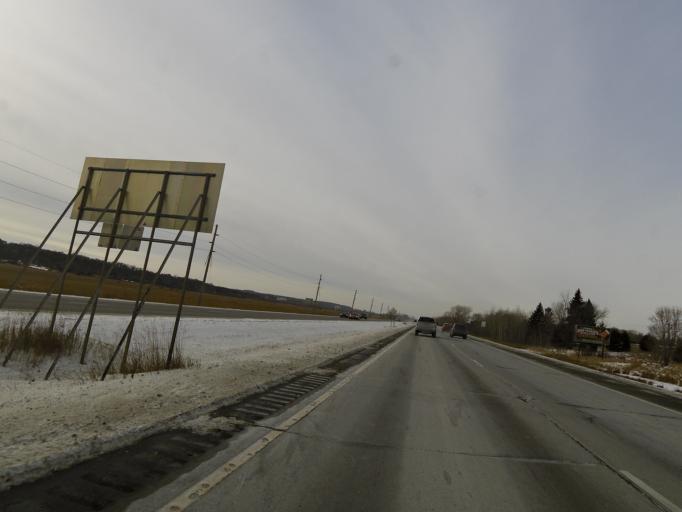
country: US
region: Minnesota
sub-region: Scott County
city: Jordan
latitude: 44.6695
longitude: -93.6429
